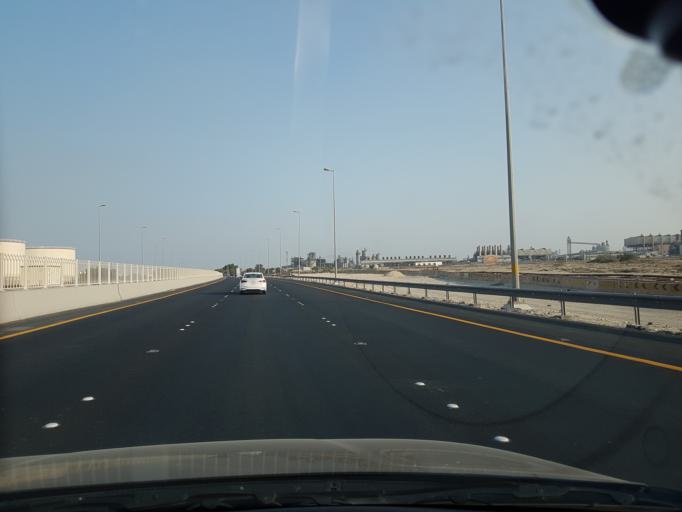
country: BH
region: Northern
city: Ar Rifa'
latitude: 26.1021
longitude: 50.6028
